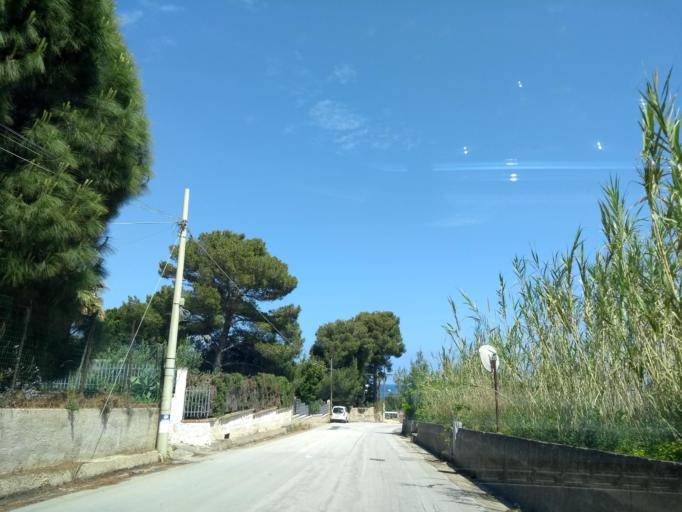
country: IT
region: Sicily
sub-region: Trapani
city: Castellammare del Golfo
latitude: 38.0525
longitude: 12.8407
